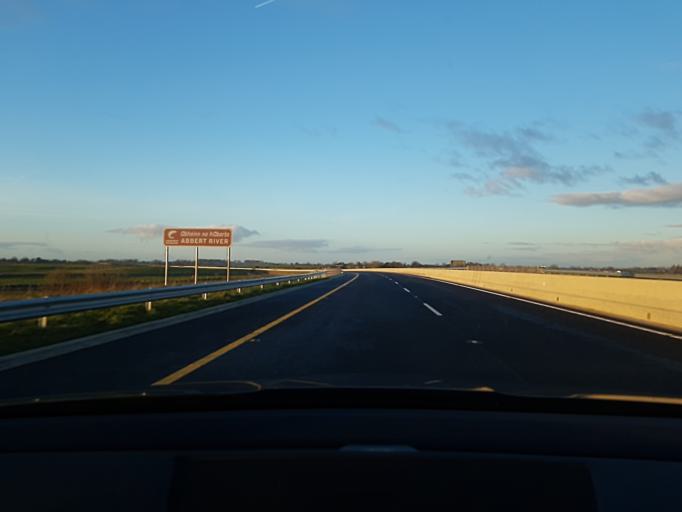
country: IE
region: Connaught
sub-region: County Galway
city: Tuam
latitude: 53.4195
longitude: -8.8297
